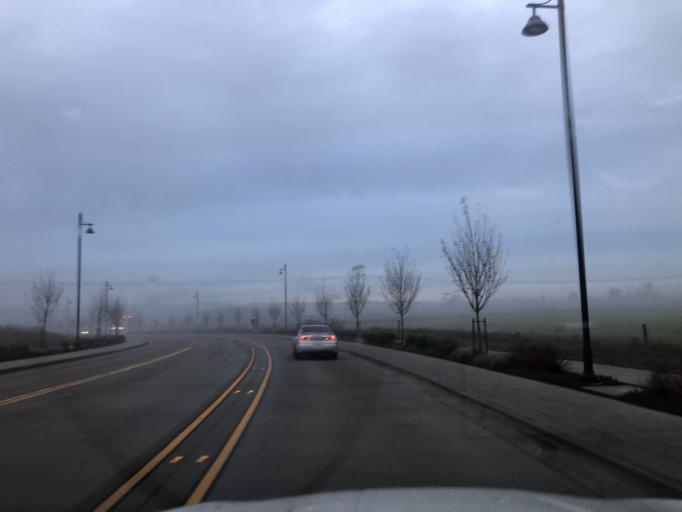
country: US
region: Oregon
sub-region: Washington County
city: Aloha
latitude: 45.4927
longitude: -122.8958
